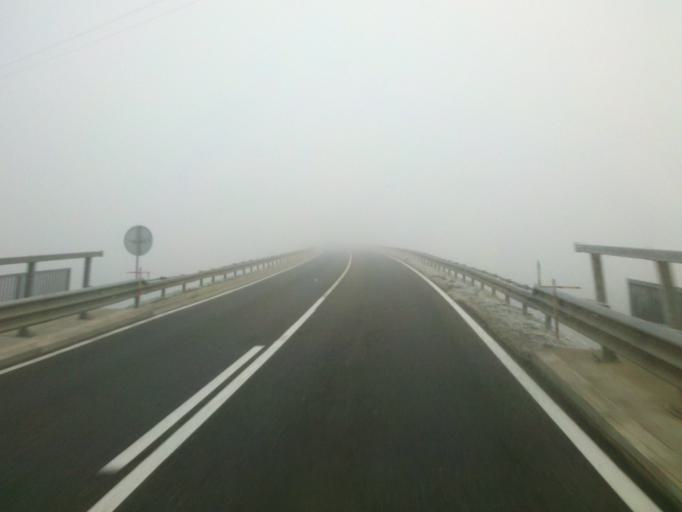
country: HR
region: Varazdinska
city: Jalkovec
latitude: 46.2835
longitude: 16.3103
